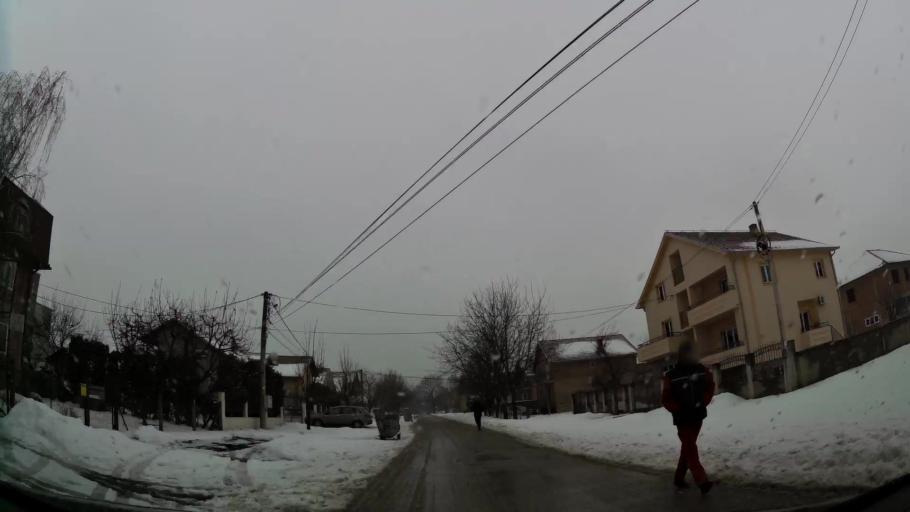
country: RS
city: Novi Banovci
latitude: 44.8773
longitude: 20.3167
